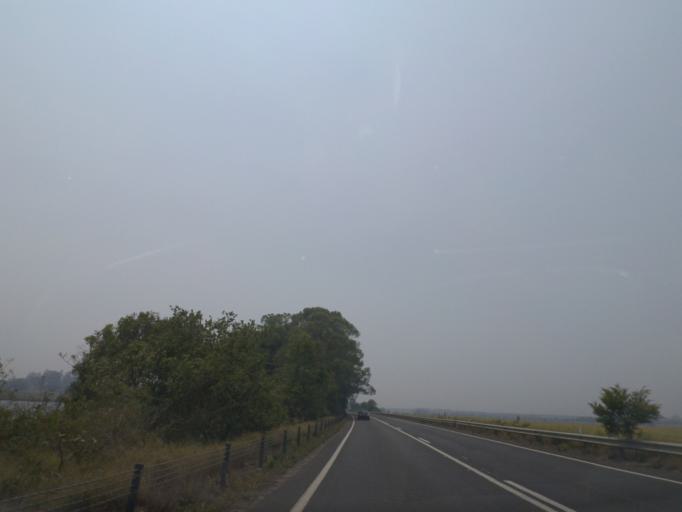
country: AU
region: New South Wales
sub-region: Clarence Valley
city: Maclean
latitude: -29.5416
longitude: 153.1664
